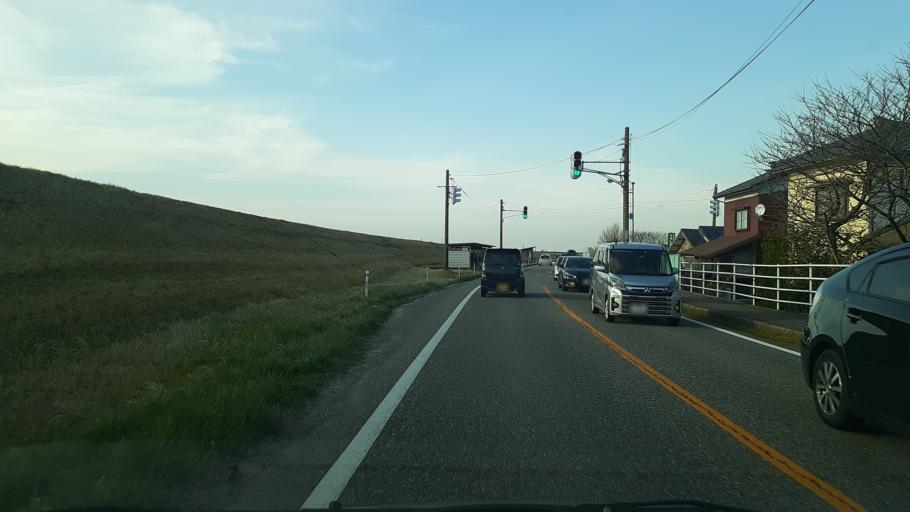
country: JP
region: Niigata
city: Niigata-shi
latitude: 37.8556
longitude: 139.0246
